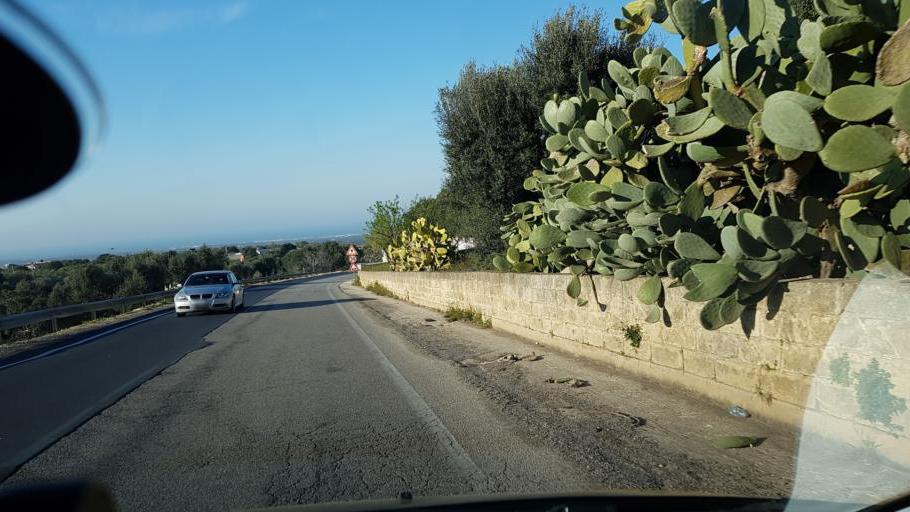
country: IT
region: Apulia
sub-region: Provincia di Brindisi
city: Ostuni
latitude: 40.7304
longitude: 17.5901
